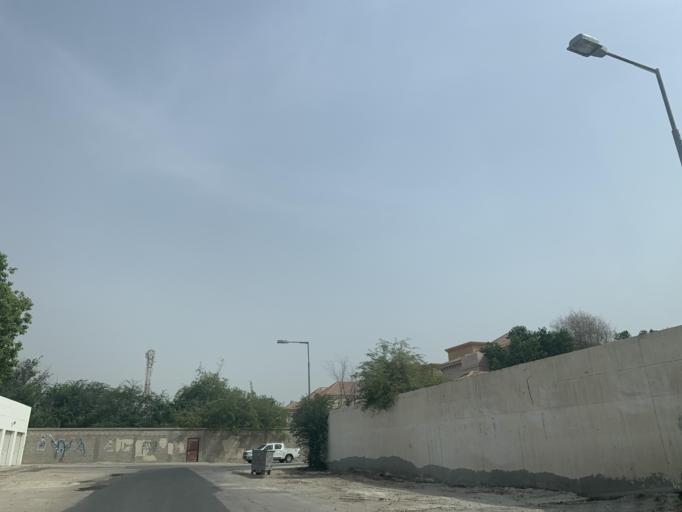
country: BH
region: Manama
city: Jidd Hafs
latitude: 26.2005
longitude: 50.4802
